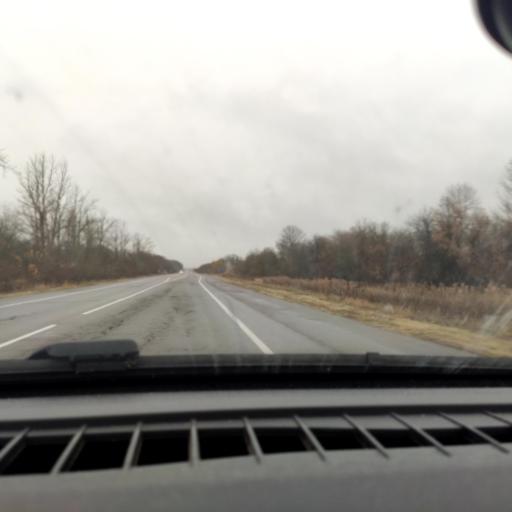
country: RU
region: Voronezj
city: Kolodeznyy
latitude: 51.2912
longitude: 39.0402
